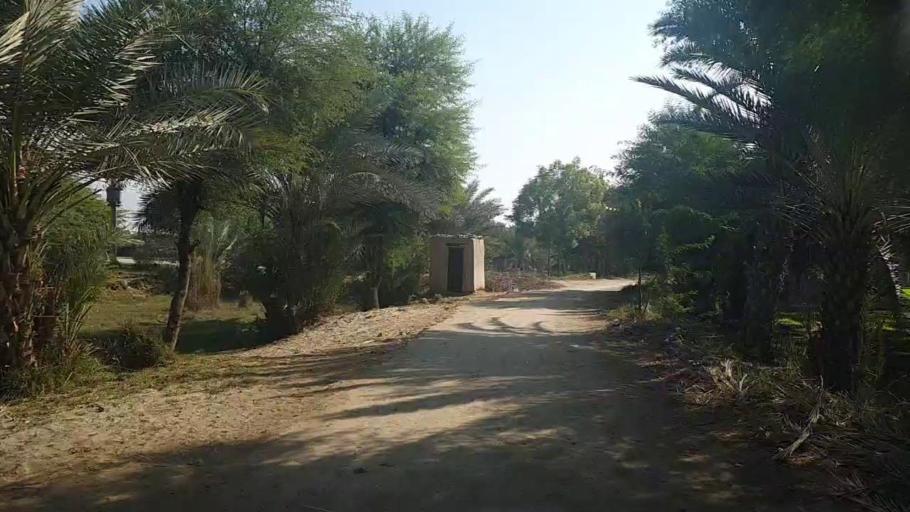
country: PK
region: Sindh
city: Kot Diji
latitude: 27.4328
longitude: 68.7211
